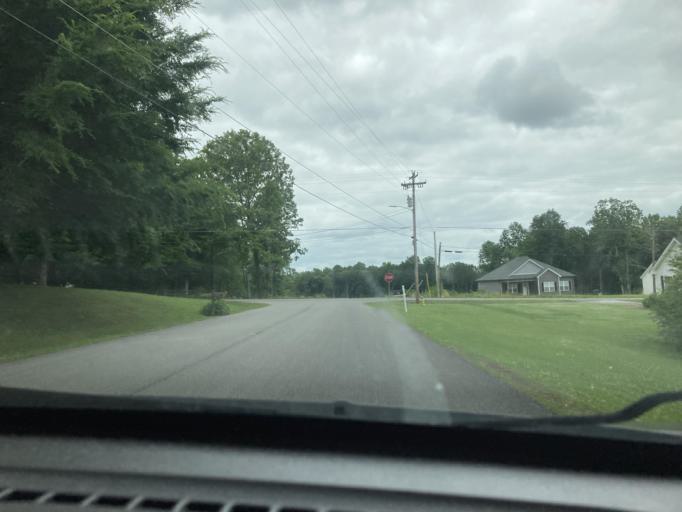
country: US
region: Tennessee
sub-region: Dickson County
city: Dickson
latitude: 36.0995
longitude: -87.3810
